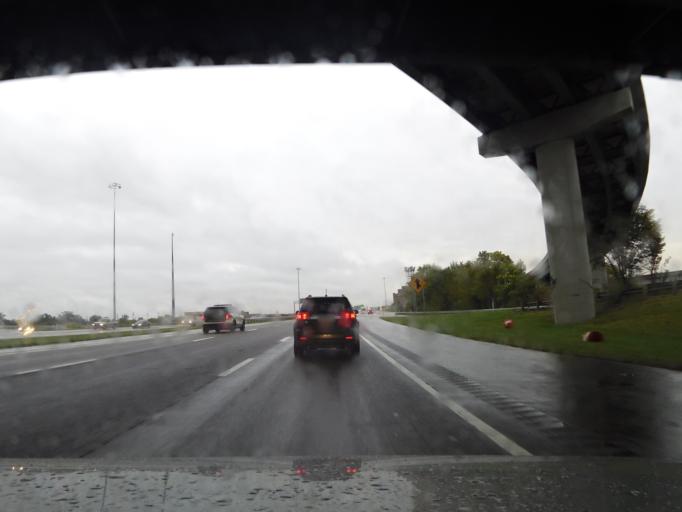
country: US
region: Tennessee
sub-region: Knox County
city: Knoxville
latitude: 35.9684
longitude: -83.9291
